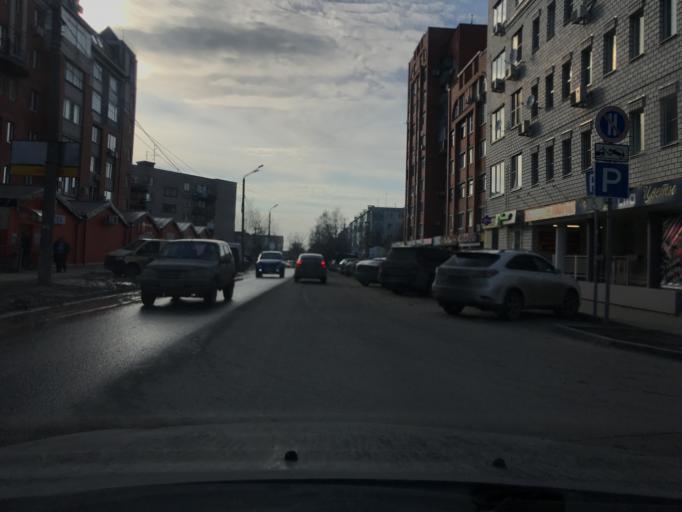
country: RU
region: Kaluga
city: Kaluga
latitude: 54.5183
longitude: 36.2433
